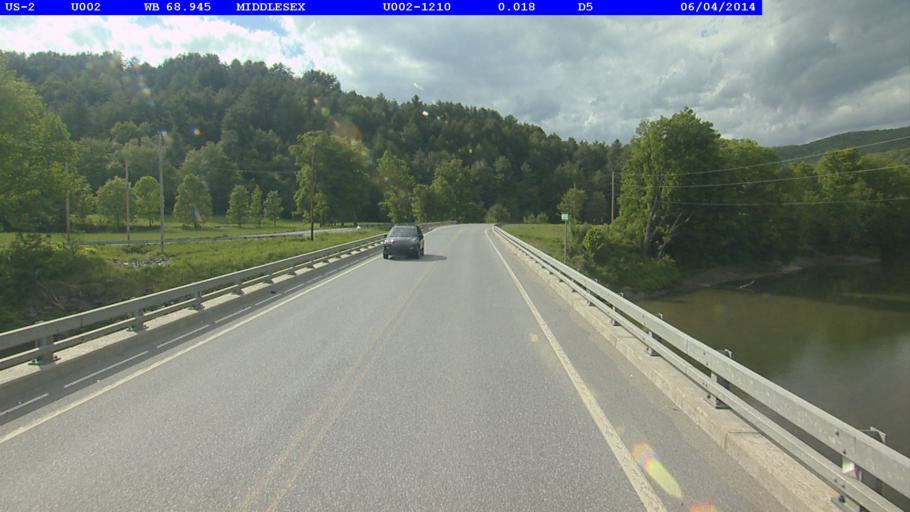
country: US
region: Vermont
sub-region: Washington County
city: Waterbury
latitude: 44.3063
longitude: -72.6957
